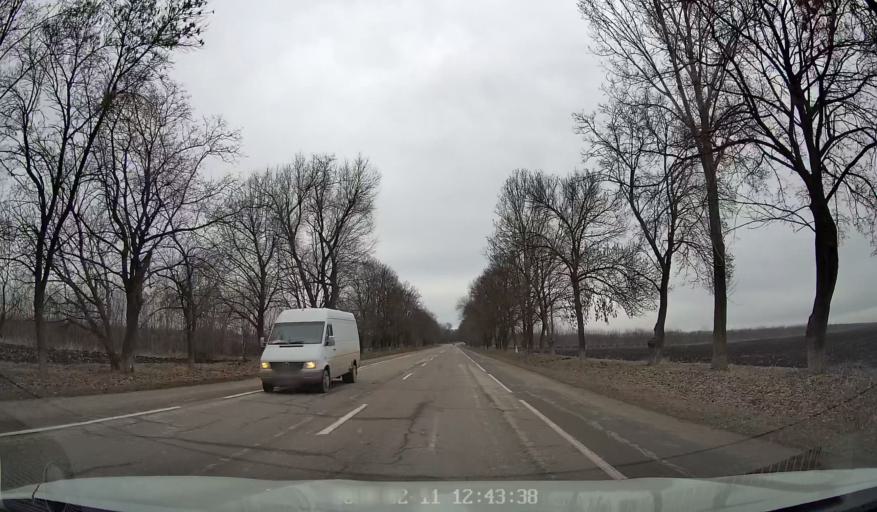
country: MD
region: Raionul Edinet
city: Edinet
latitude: 48.2355
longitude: 27.2083
